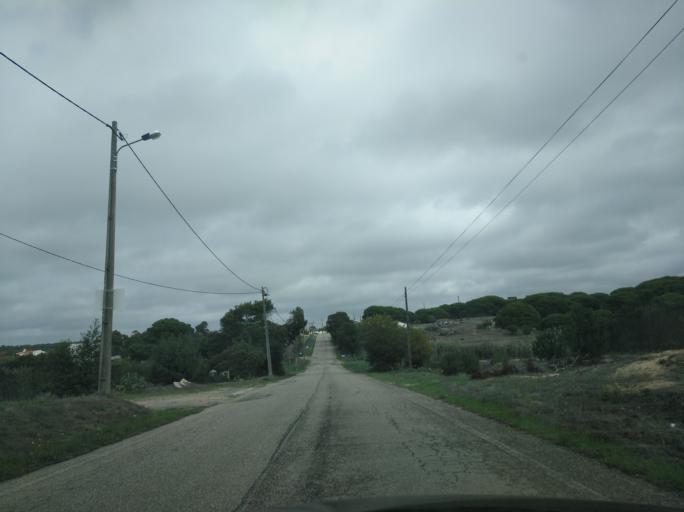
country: PT
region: Setubal
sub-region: Santiago do Cacem
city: Santo Andre
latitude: 38.1349
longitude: -8.7625
